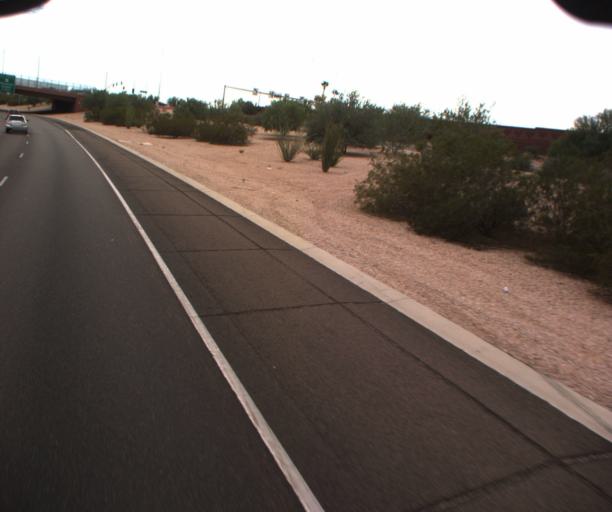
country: US
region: Arizona
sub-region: Pinal County
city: Apache Junction
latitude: 33.4097
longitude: -111.6404
